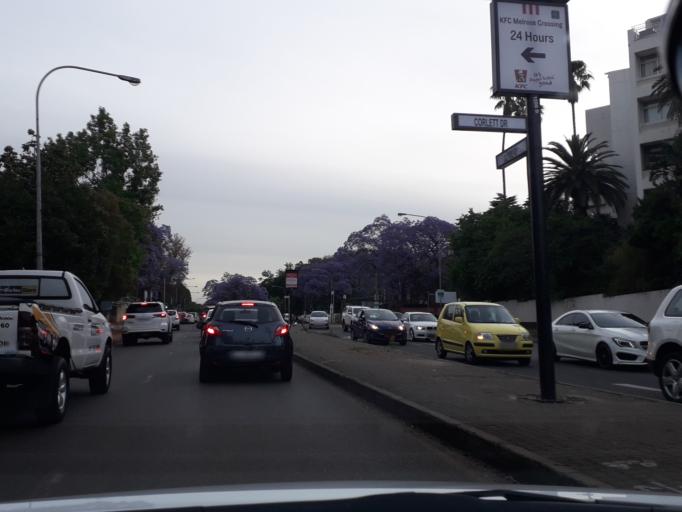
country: ZA
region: Gauteng
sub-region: City of Johannesburg Metropolitan Municipality
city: Johannesburg
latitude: -26.1354
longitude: 28.0480
